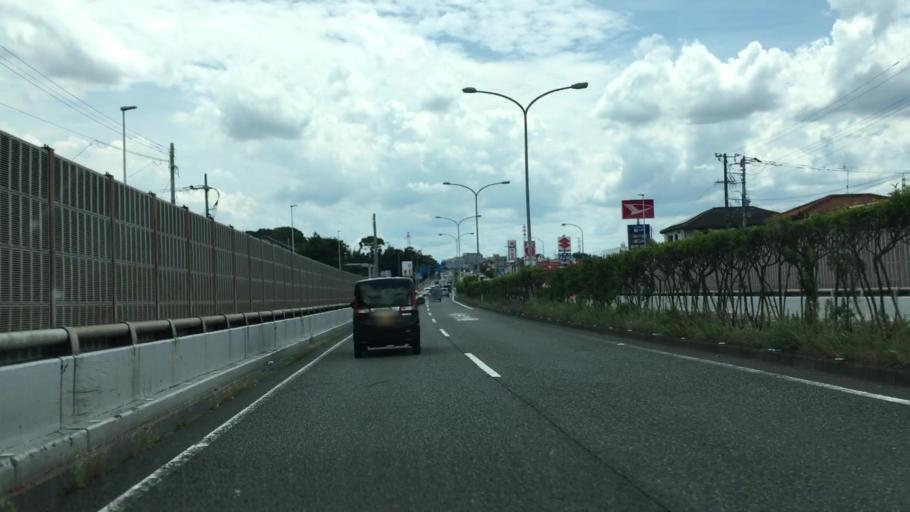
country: JP
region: Fukuoka
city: Chikushino-shi
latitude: 33.4810
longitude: 130.5387
